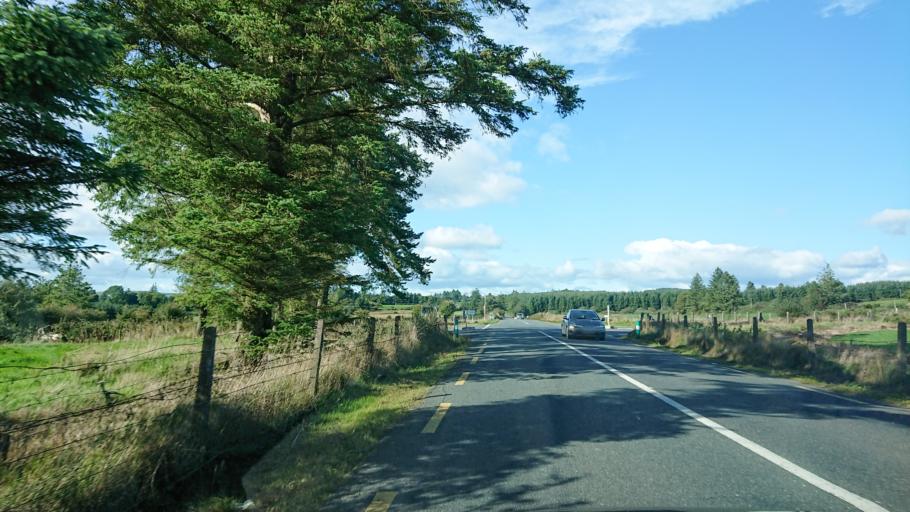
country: IE
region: Munster
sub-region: Waterford
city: Dungarvan
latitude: 52.2014
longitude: -7.7012
